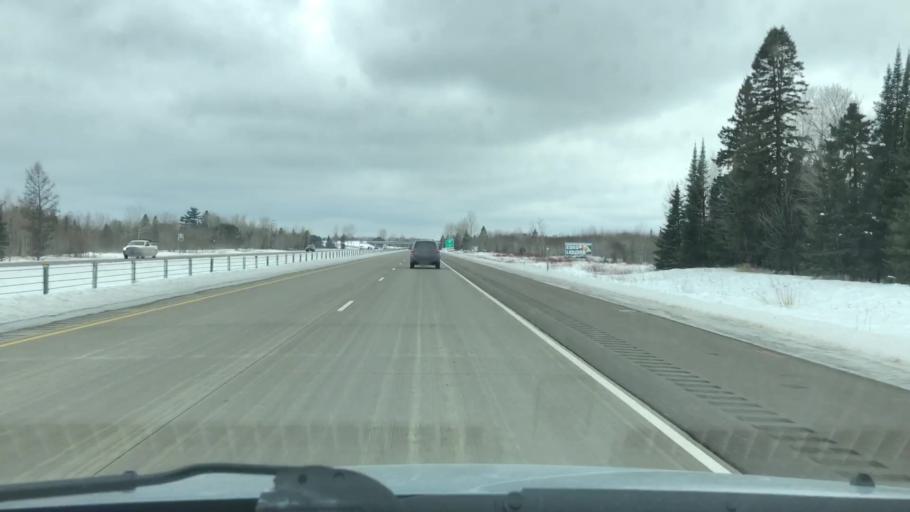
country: US
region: Minnesota
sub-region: Carlton County
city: Esko
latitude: 46.6967
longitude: -92.3535
